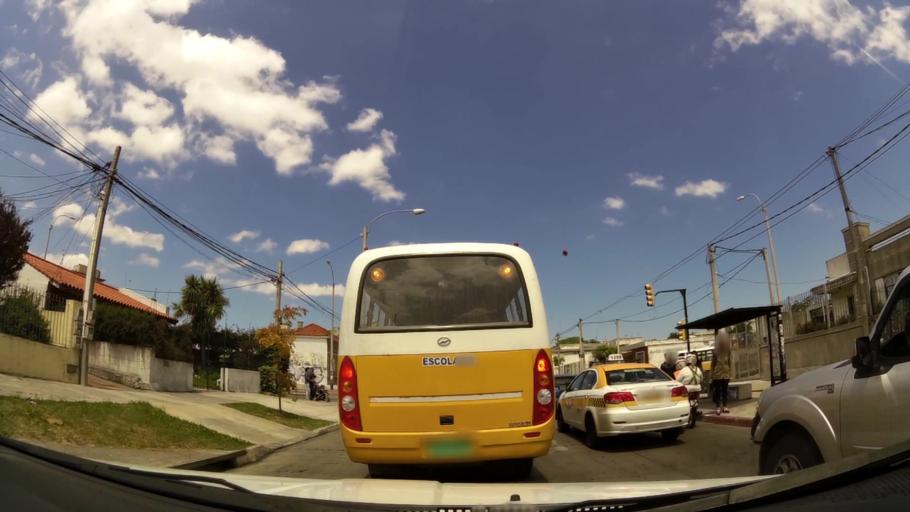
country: UY
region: Montevideo
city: Montevideo
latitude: -34.8531
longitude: -56.2254
